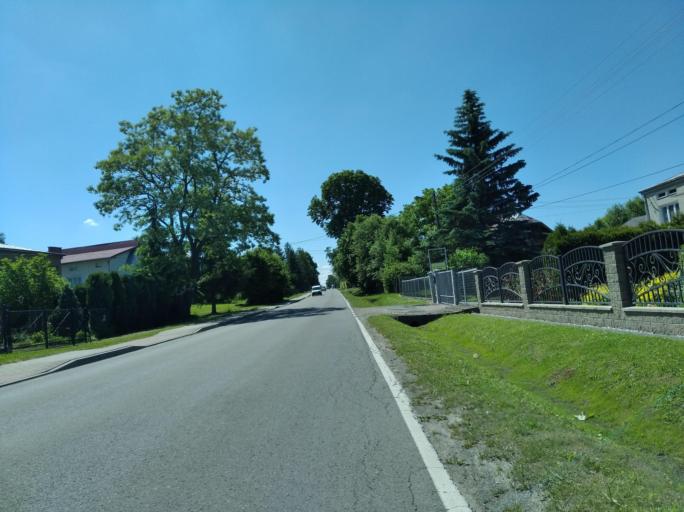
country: PL
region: Subcarpathian Voivodeship
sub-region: Powiat krosnienski
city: Chorkowka
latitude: 49.6619
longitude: 21.6928
